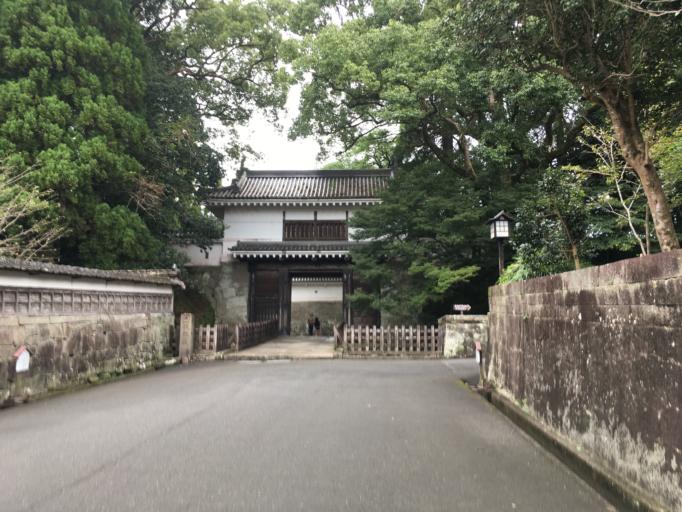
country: JP
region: Miyazaki
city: Nichinan
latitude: 31.6273
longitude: 131.3520
